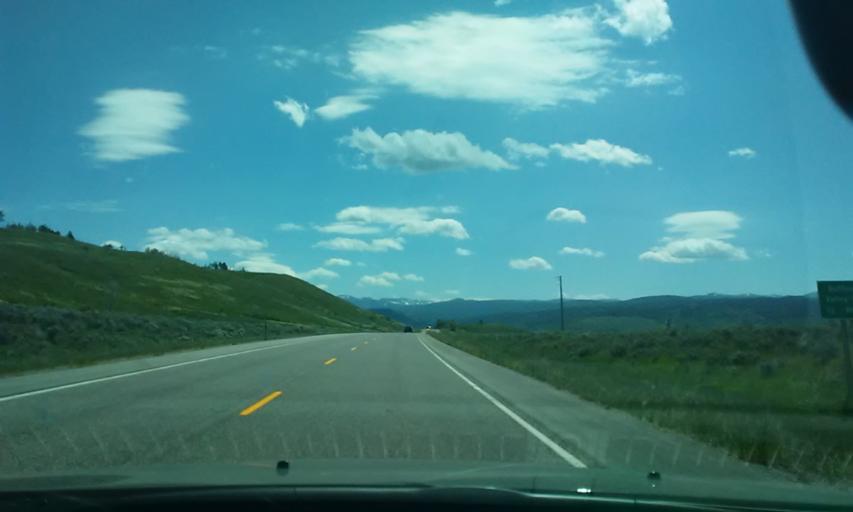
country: US
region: Wyoming
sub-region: Teton County
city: Jackson
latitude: 43.8400
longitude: -110.4554
